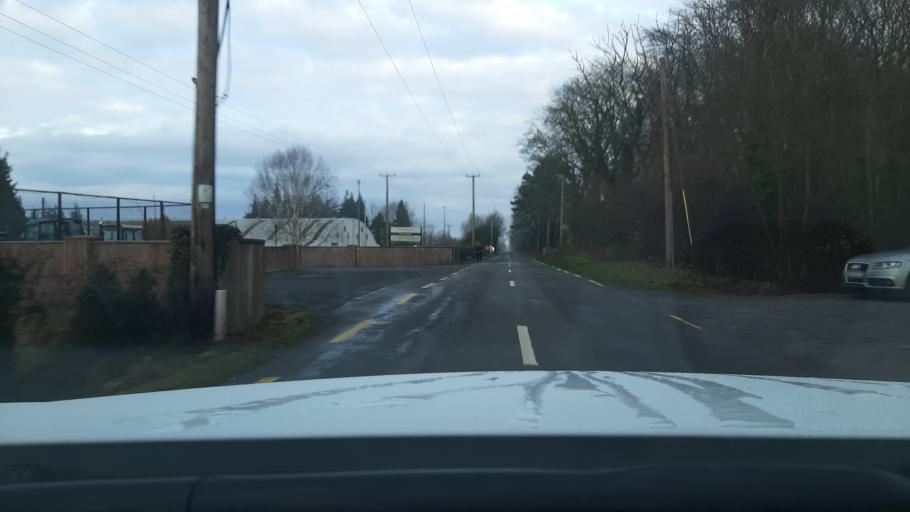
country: IE
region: Leinster
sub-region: Kildare
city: Rathangan
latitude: 53.2400
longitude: -7.0107
